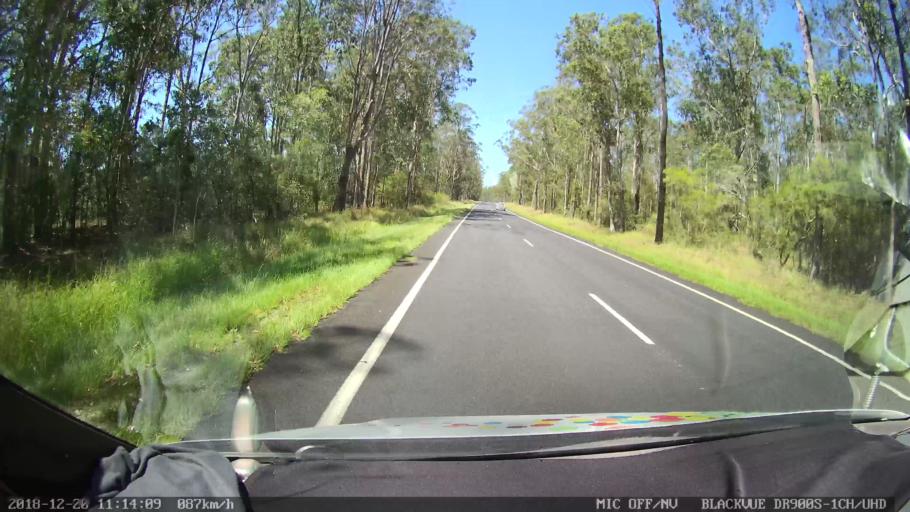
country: AU
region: New South Wales
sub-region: Richmond Valley
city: Casino
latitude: -28.9971
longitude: 153.0102
